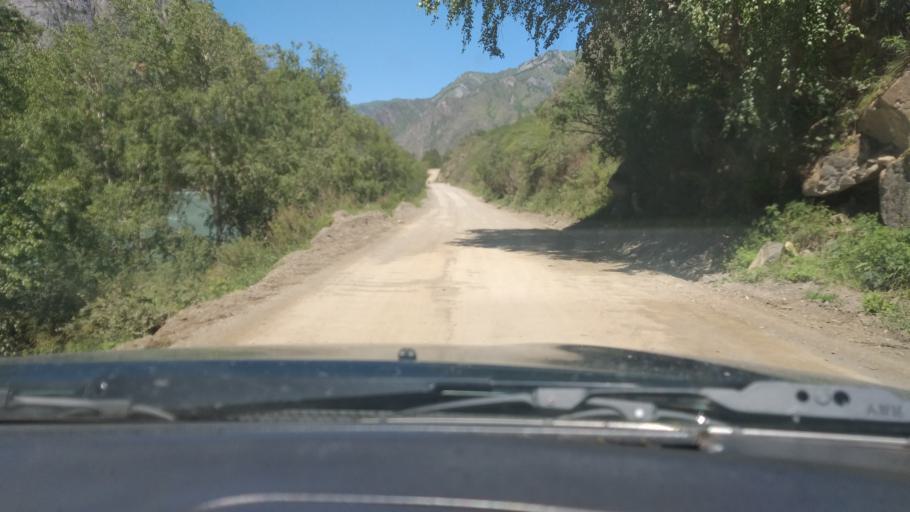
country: RU
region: Altay
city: Chemal
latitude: 51.2035
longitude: 86.0852
